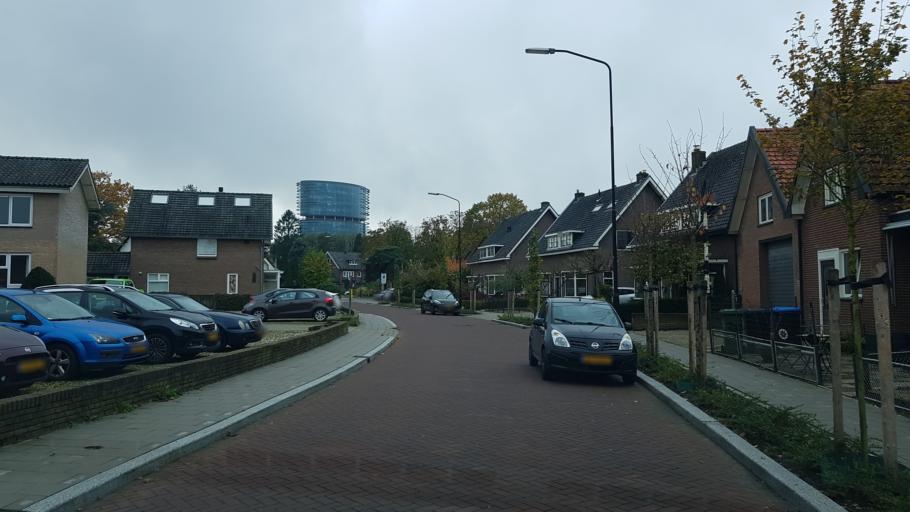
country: NL
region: Gelderland
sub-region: Gemeente Apeldoorn
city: Apeldoorn
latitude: 52.2157
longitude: 5.9418
